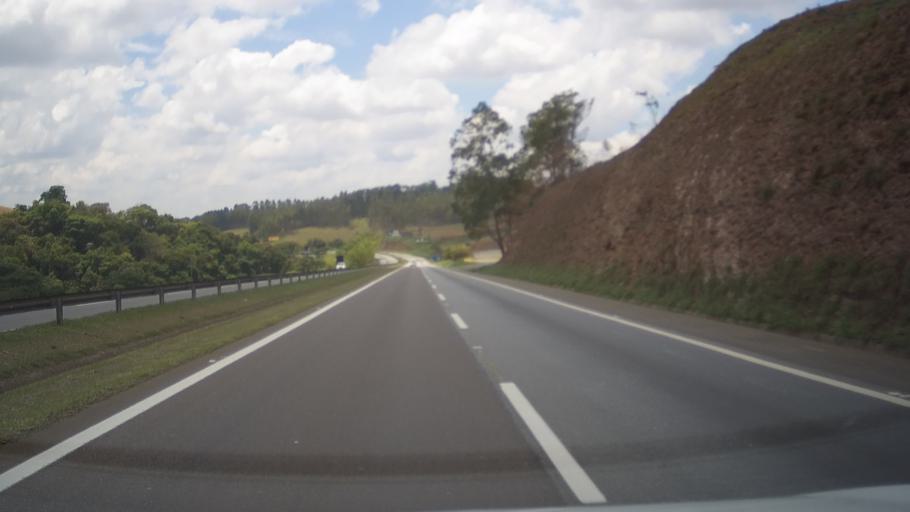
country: BR
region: Minas Gerais
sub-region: Tres Coracoes
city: Tres Coracoes
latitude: -21.6955
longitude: -45.3588
